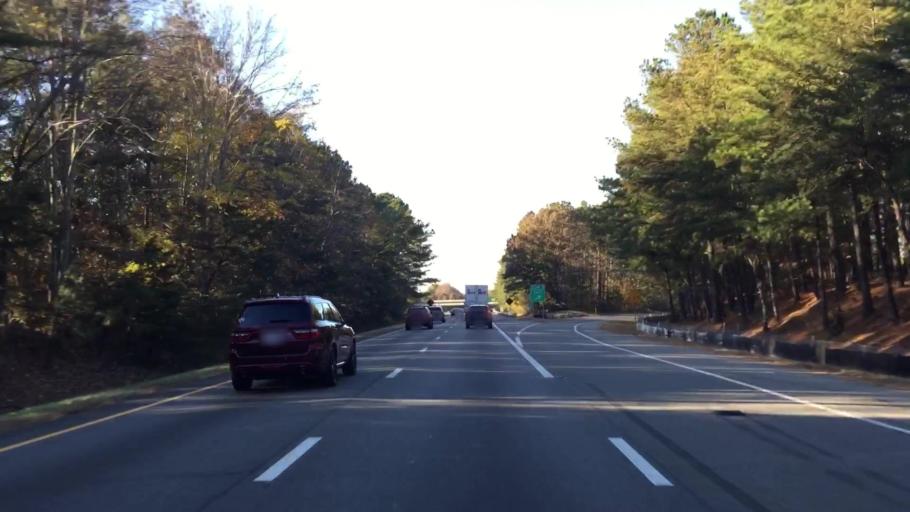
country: US
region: Virginia
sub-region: James City County
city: Williamsburg
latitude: 37.3491
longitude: -76.7270
